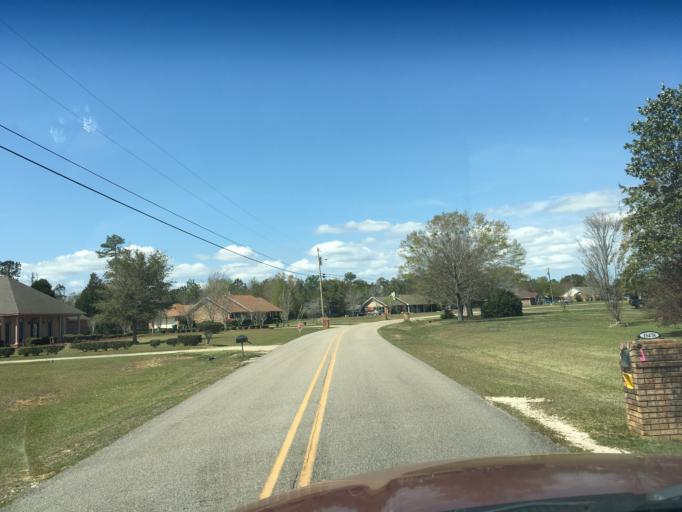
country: US
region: Mississippi
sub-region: Jackson County
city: Latimer
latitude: 30.5124
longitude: -88.9750
